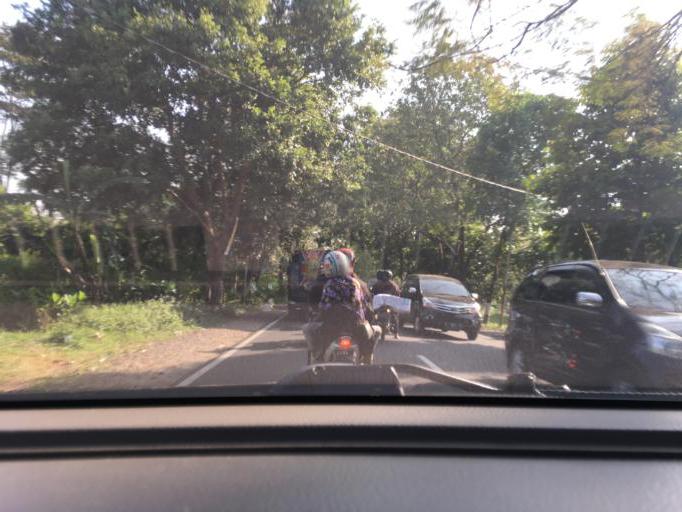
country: ID
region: West Java
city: Kuningan
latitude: -6.9002
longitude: 108.4910
